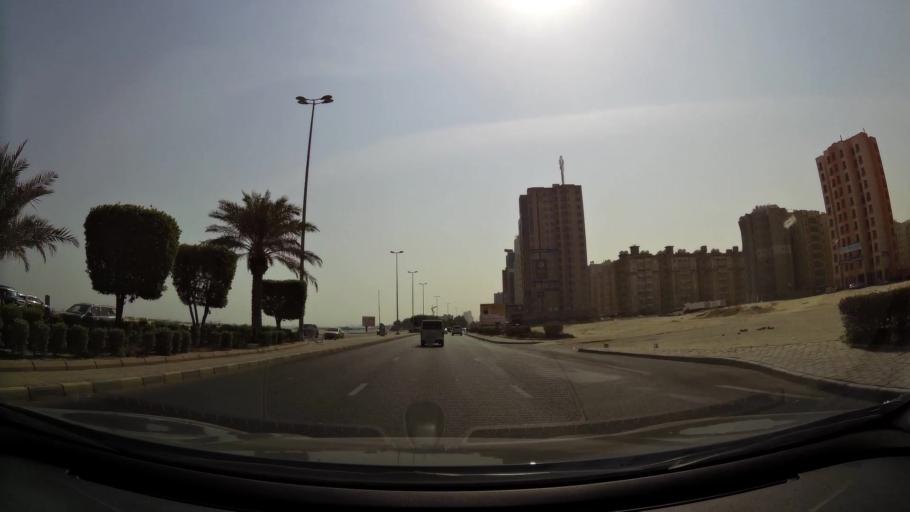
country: KW
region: Al Ahmadi
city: Al Manqaf
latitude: 29.1040
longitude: 48.1375
